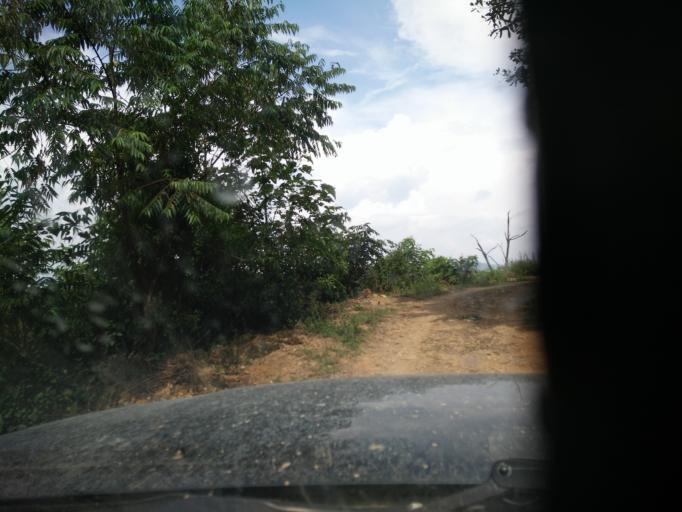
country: CN
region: Guangxi Zhuangzu Zizhiqu
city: Leli
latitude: 24.7690
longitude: 105.9037
